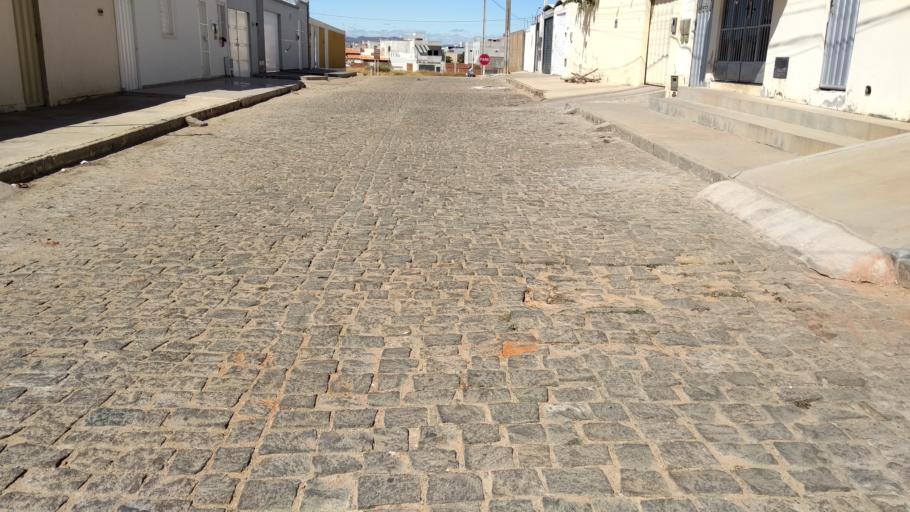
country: BR
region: Bahia
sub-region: Guanambi
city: Guanambi
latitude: -14.2379
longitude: -42.7726
